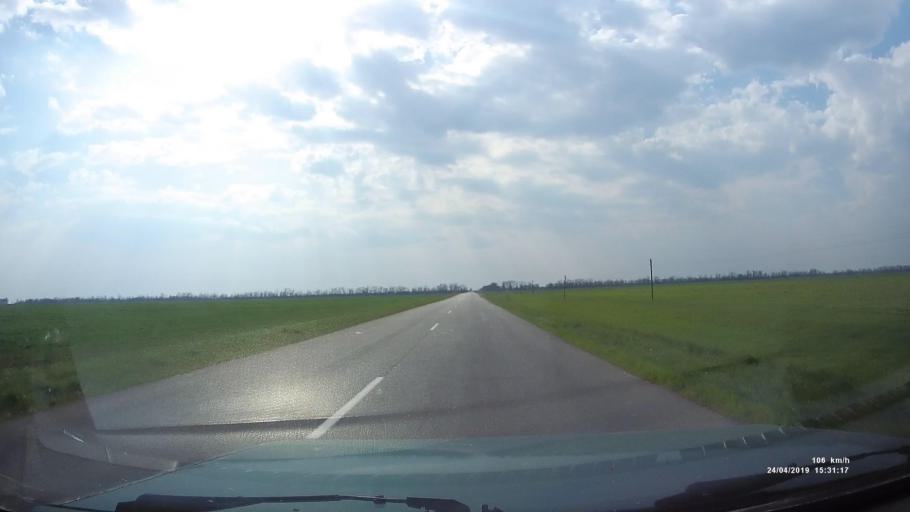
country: RU
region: Rostov
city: Remontnoye
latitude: 46.5997
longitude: 42.9869
